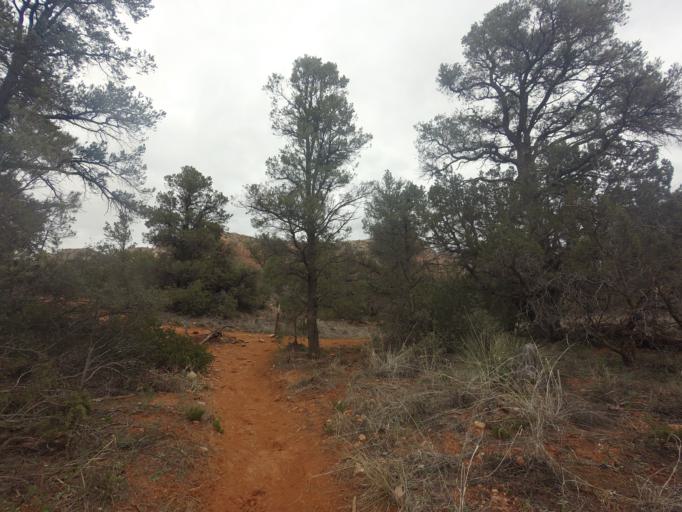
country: US
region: Arizona
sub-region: Yavapai County
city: Village of Oak Creek (Big Park)
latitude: 34.7997
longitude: -111.7477
